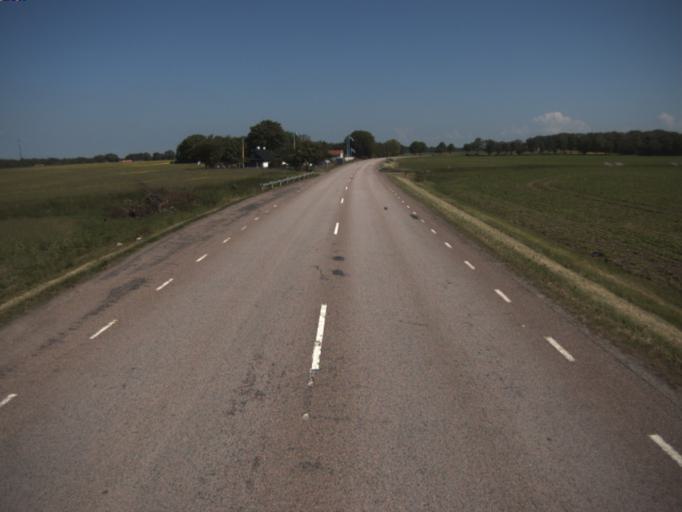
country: SE
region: Skane
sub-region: Helsingborg
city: Barslov
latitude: 56.0342
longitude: 12.7909
